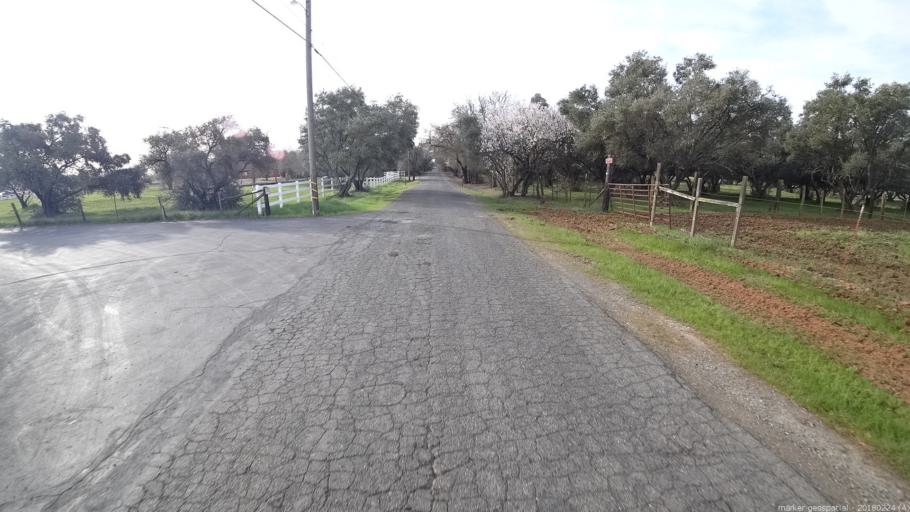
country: US
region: California
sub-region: Sacramento County
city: Rio Linda
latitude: 38.6752
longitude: -121.4708
